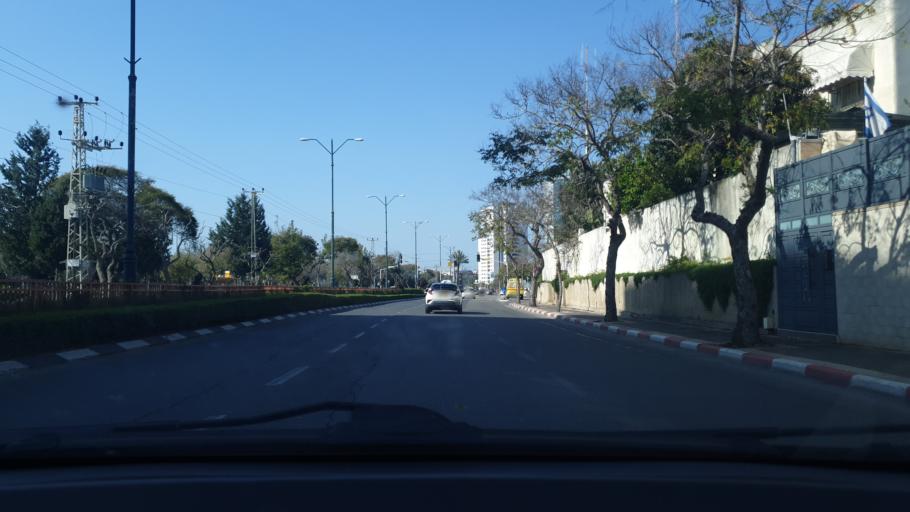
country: IL
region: Central District
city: Rishon LeZiyyon
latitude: 31.9730
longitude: 34.7976
